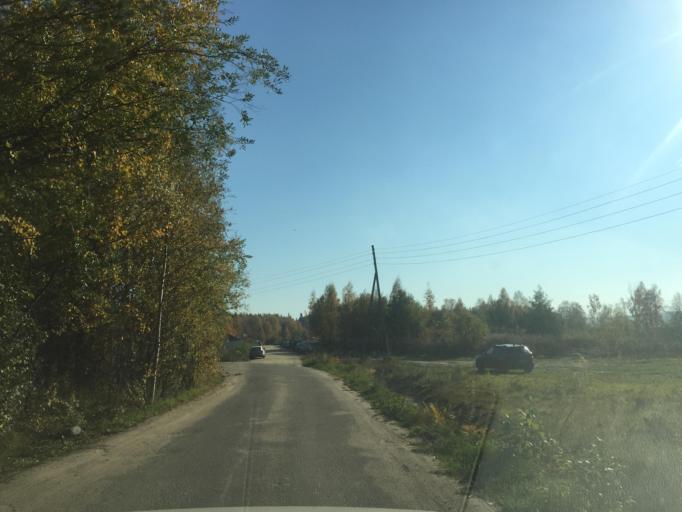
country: RU
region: Leningrad
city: Priozersk
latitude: 61.2885
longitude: 30.0859
